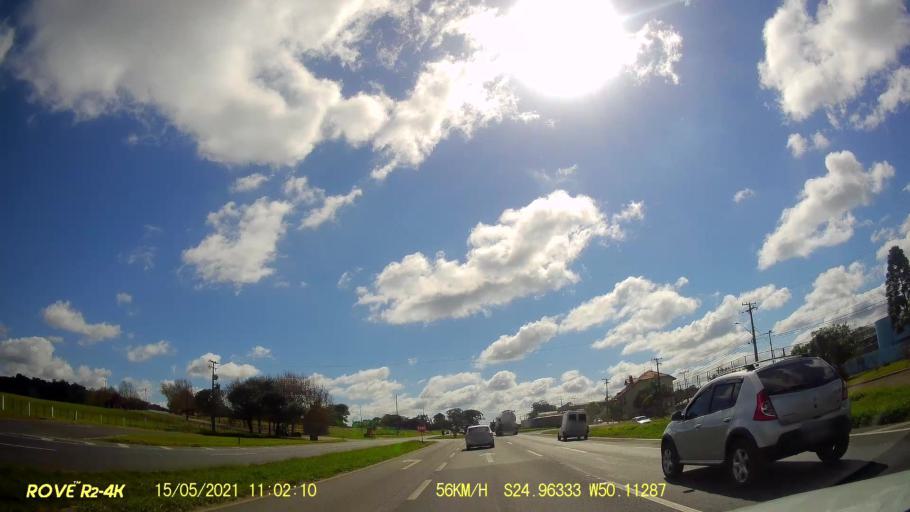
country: BR
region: Parana
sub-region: Carambei
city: Carambei
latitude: -24.9634
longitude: -50.1128
